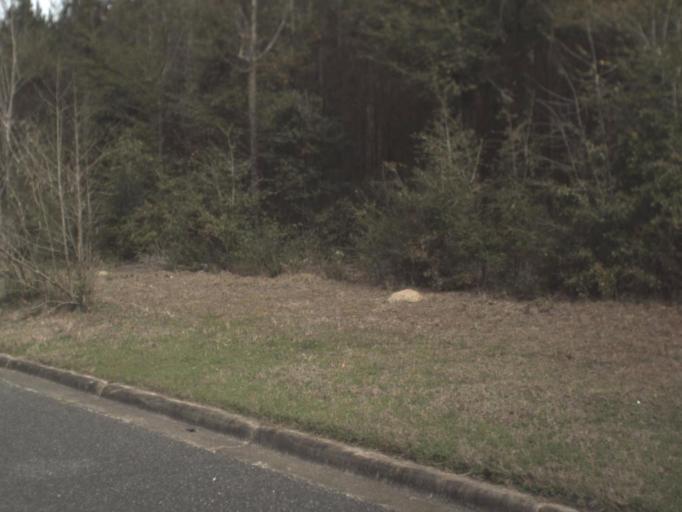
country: US
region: Florida
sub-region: Gadsden County
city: Midway
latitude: 30.4666
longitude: -84.3983
